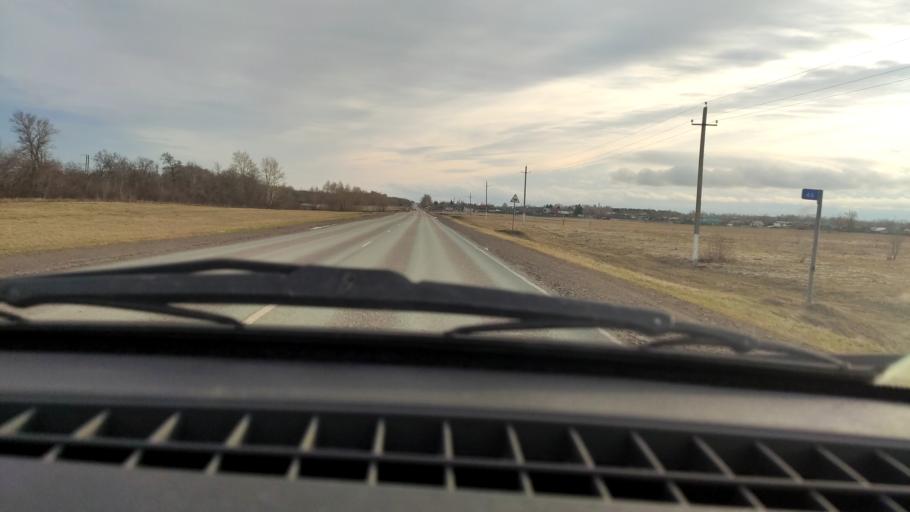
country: RU
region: Bashkortostan
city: Davlekanovo
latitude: 54.3049
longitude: 55.1371
